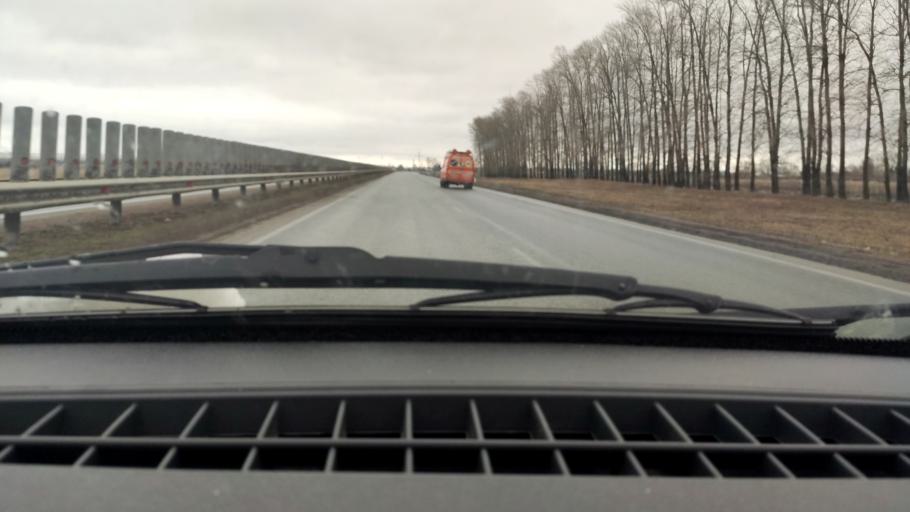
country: RU
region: Bashkortostan
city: Asanovo
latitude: 55.0083
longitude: 55.4871
